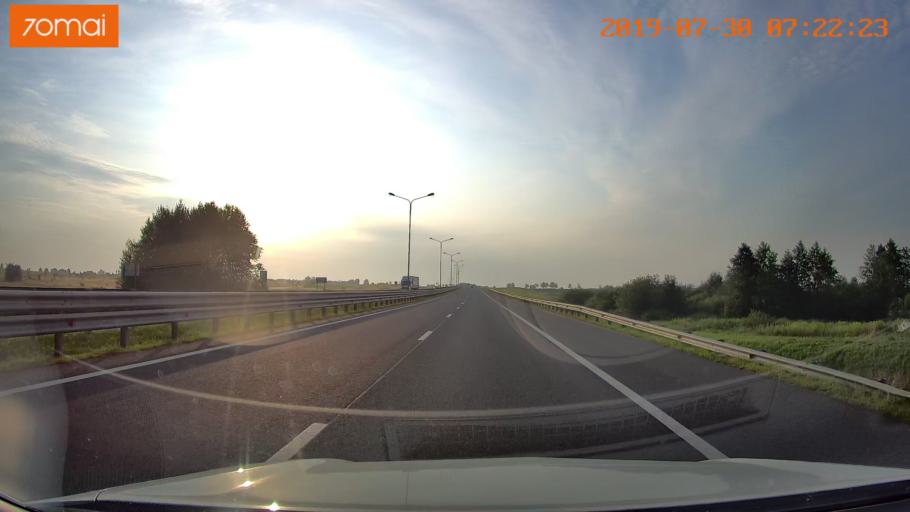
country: RU
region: Kaliningrad
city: Bol'shoe Isakovo
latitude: 54.6929
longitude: 20.7540
